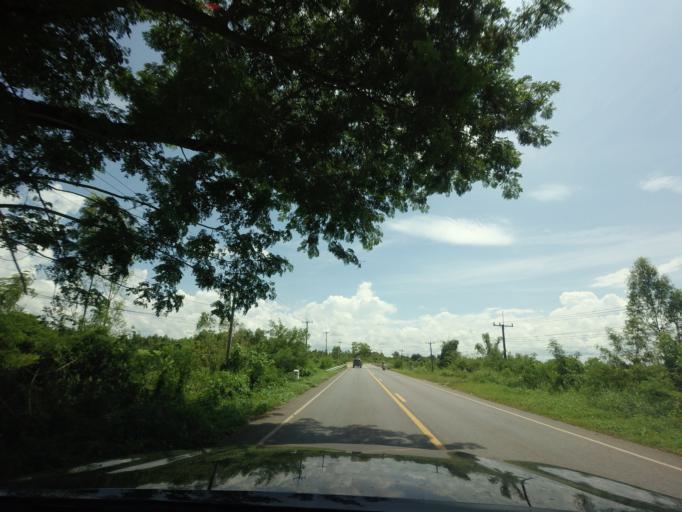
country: TH
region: Changwat Udon Thani
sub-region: Amphoe Ban Phue
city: Ban Phue
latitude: 17.7154
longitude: 102.4099
